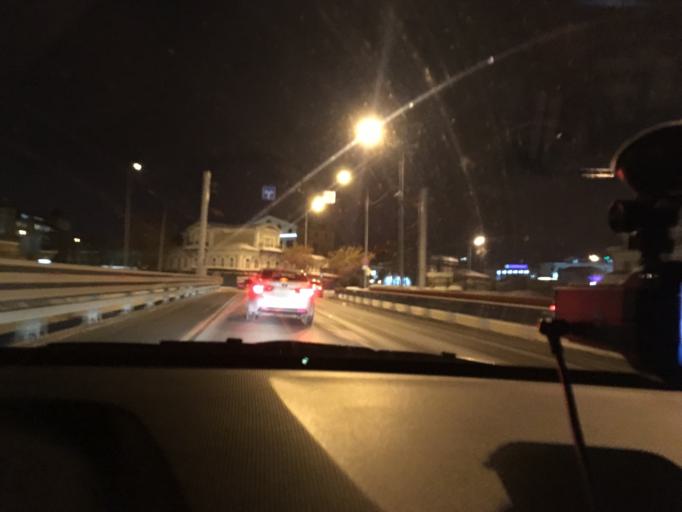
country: RU
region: Tjumen
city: Tyumen
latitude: 57.1614
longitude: 65.5407
